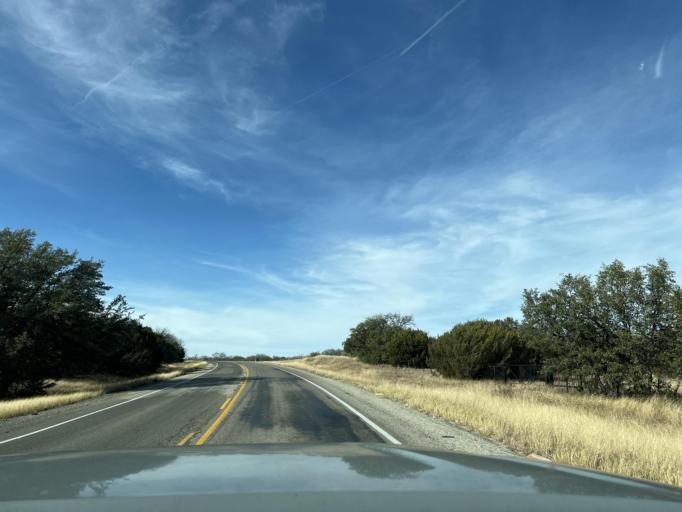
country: US
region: Texas
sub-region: Eastland County
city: Cisco
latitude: 32.4578
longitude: -98.9903
